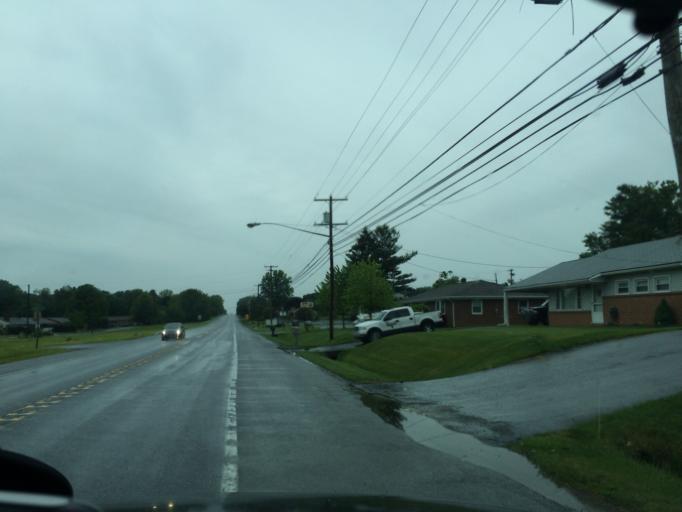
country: US
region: Maryland
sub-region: Washington County
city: Cavetown
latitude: 39.6437
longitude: -77.6007
